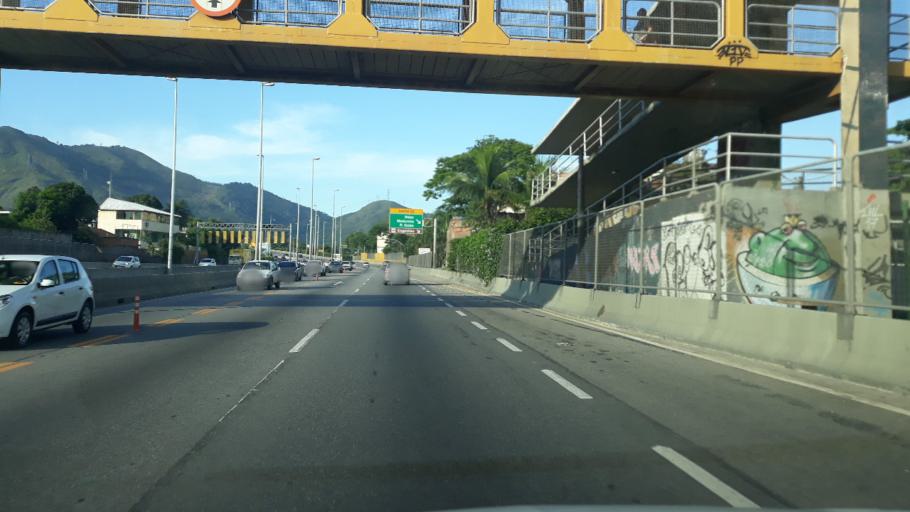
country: BR
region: Rio de Janeiro
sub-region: Rio De Janeiro
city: Rio de Janeiro
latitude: -22.8907
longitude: -43.2973
